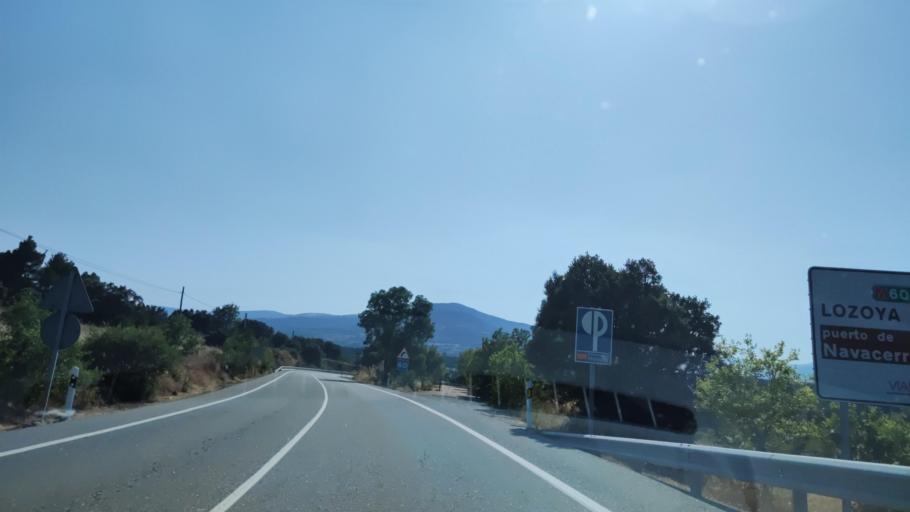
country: ES
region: Madrid
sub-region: Provincia de Madrid
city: Garganta de los Montes
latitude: 40.9436
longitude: -3.7132
